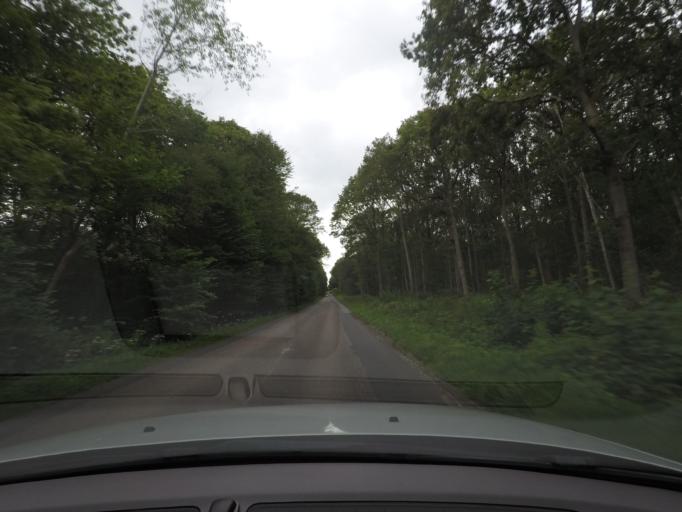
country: FR
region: Haute-Normandie
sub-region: Departement de l'Eure
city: Le Manoir
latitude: 49.3333
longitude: 1.2020
